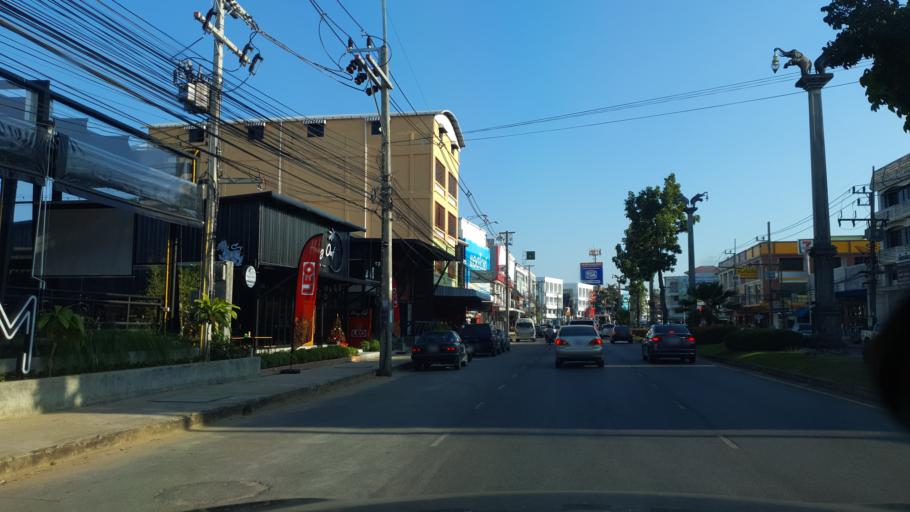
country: TH
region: Krabi
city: Krabi
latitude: 8.0683
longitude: 98.9141
